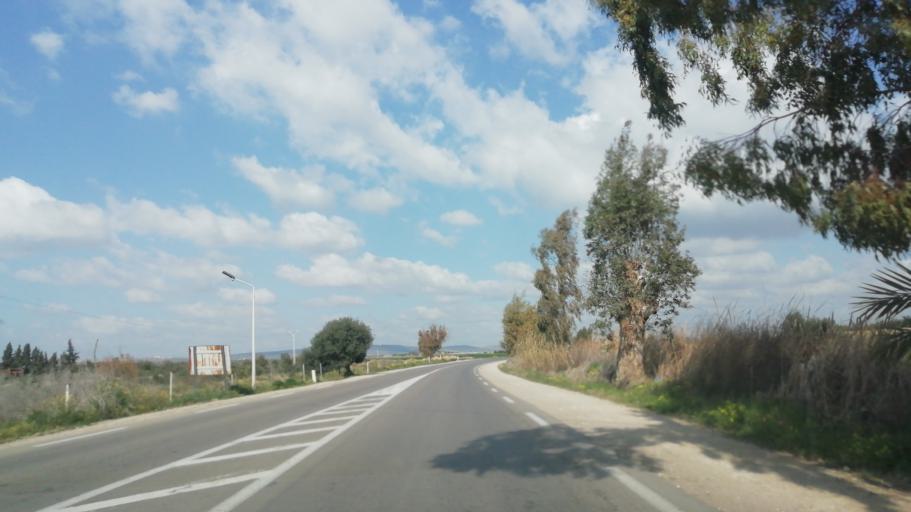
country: DZ
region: Mostaganem
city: Mostaganem
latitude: 35.6911
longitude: 0.2119
